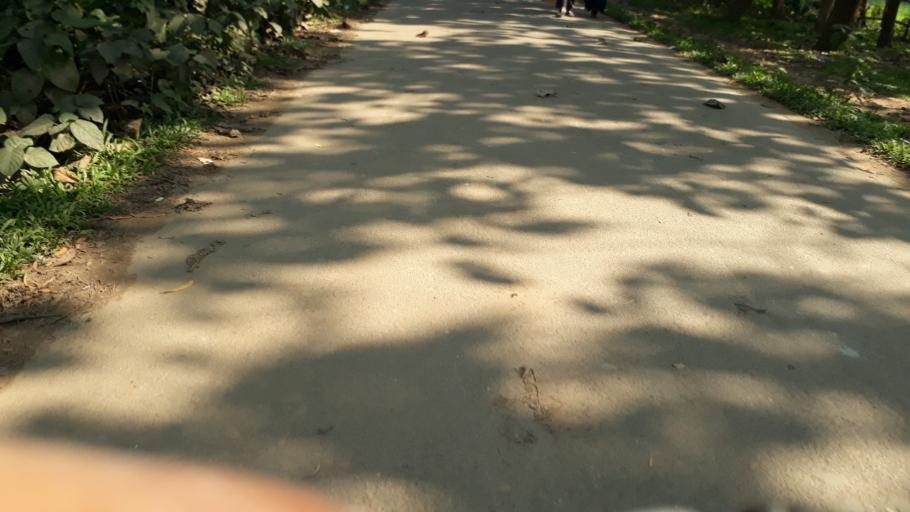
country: BD
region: Dhaka
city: Tungi
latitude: 23.8798
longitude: 90.2621
